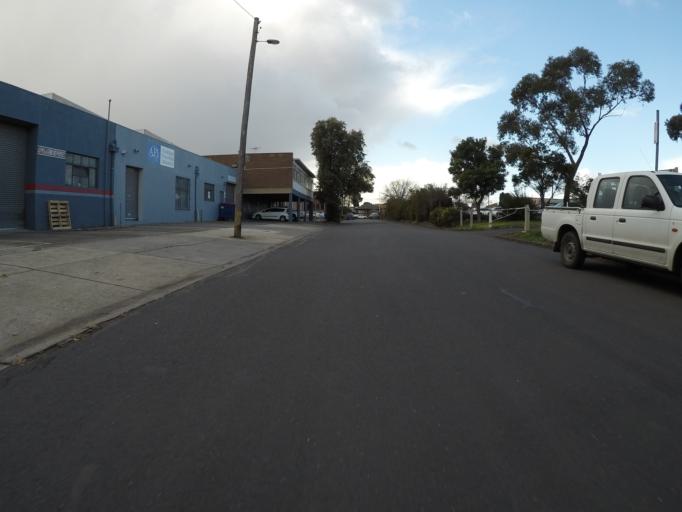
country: AU
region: Victoria
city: Brunswick East
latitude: -37.7696
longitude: 144.9745
